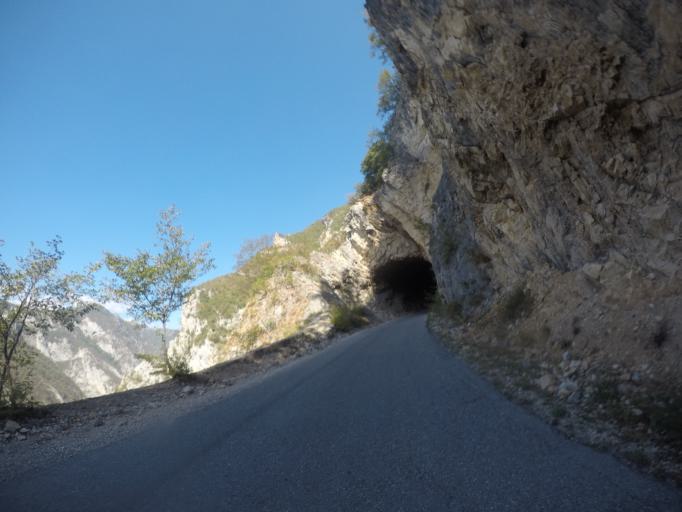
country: ME
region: Opstina Pluzine
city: Pluzine
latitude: 43.1692
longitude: 18.8590
